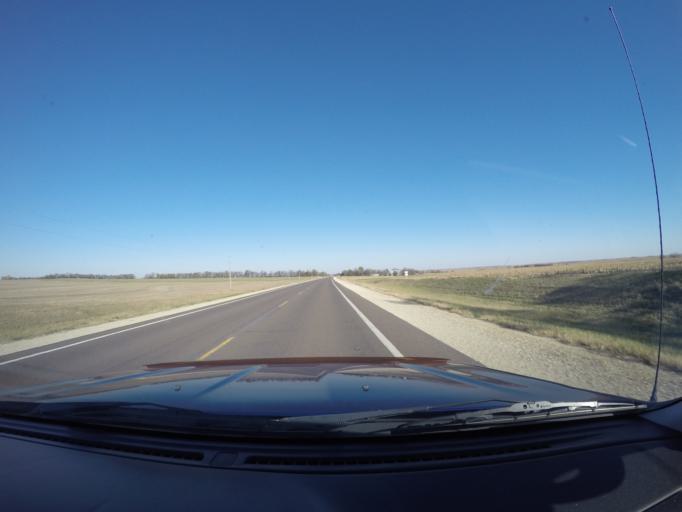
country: US
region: Kansas
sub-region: Marshall County
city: Blue Rapids
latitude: 39.5985
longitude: -96.7501
